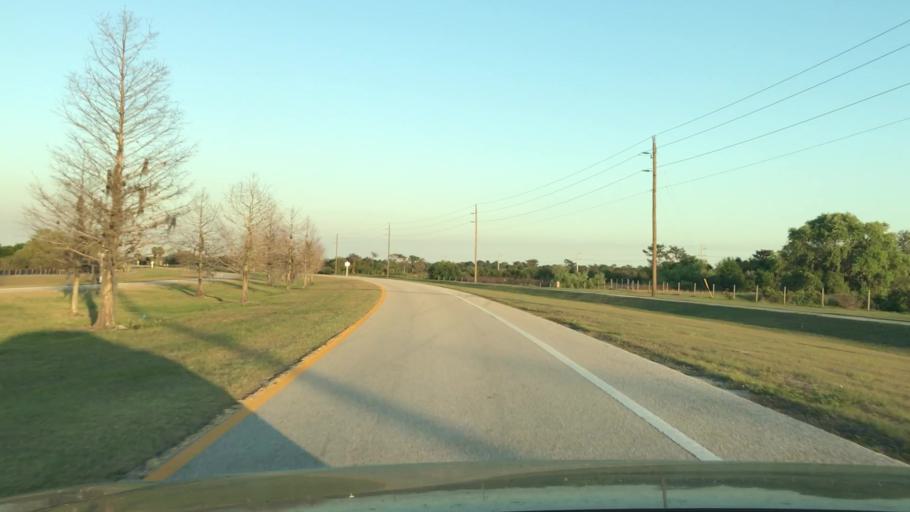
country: US
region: Florida
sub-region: Sarasota County
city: The Meadows
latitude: 27.3858
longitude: -82.3726
